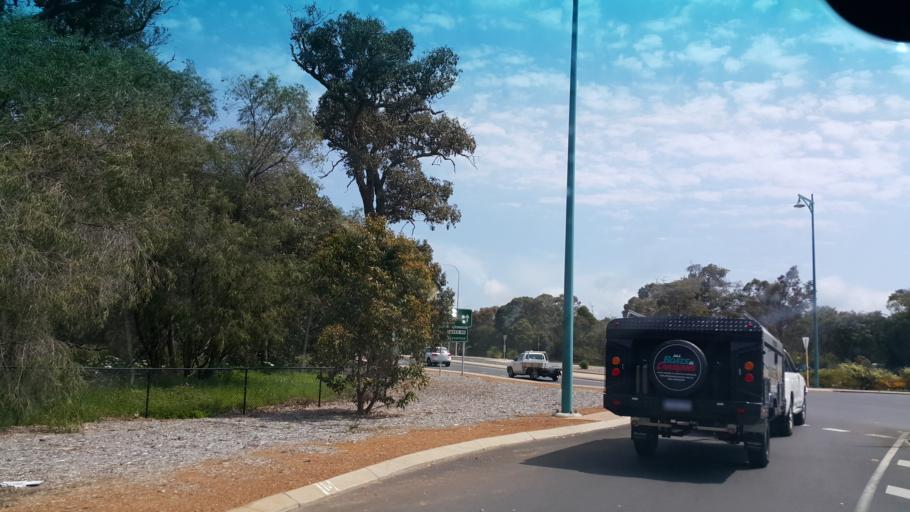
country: AU
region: Western Australia
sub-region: Busselton
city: Dunsborough
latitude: -33.6170
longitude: 115.1024
